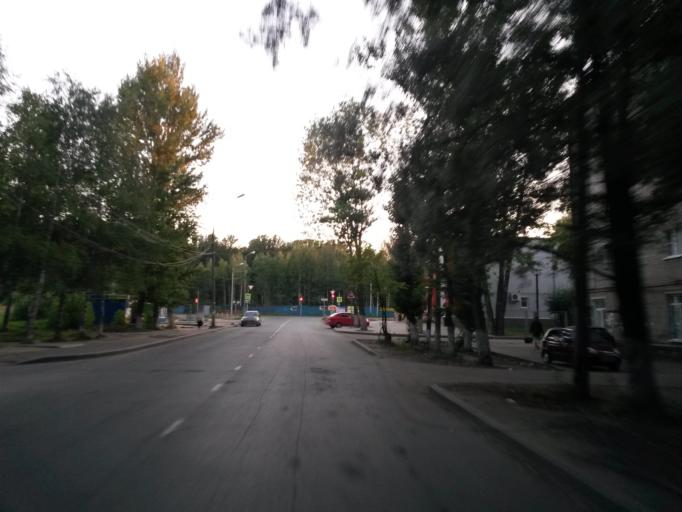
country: RU
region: Jaroslavl
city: Yaroslavl
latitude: 57.5977
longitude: 39.9106
